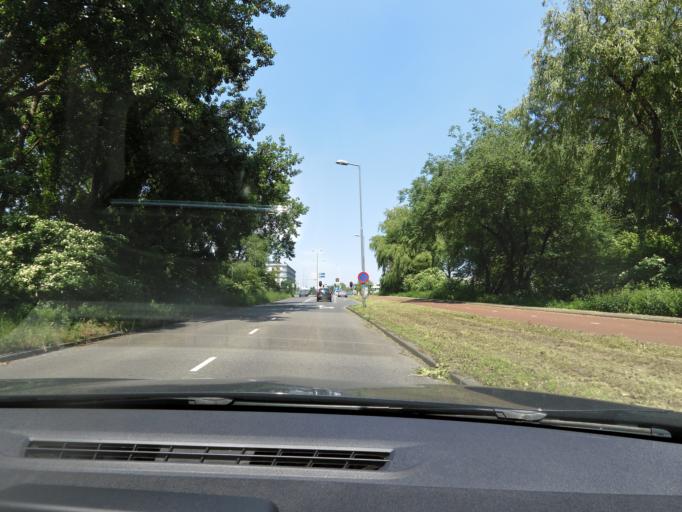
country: NL
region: South Holland
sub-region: Gemeente Rotterdam
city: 's-Gravenland
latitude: 51.9129
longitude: 4.5273
